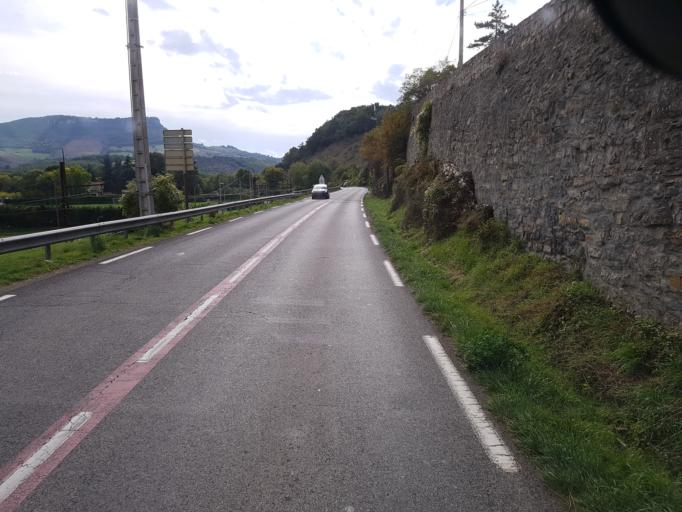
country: FR
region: Midi-Pyrenees
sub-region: Departement de l'Aveyron
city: Saint-Georges-de-Luzencon
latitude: 44.0625
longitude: 2.9828
